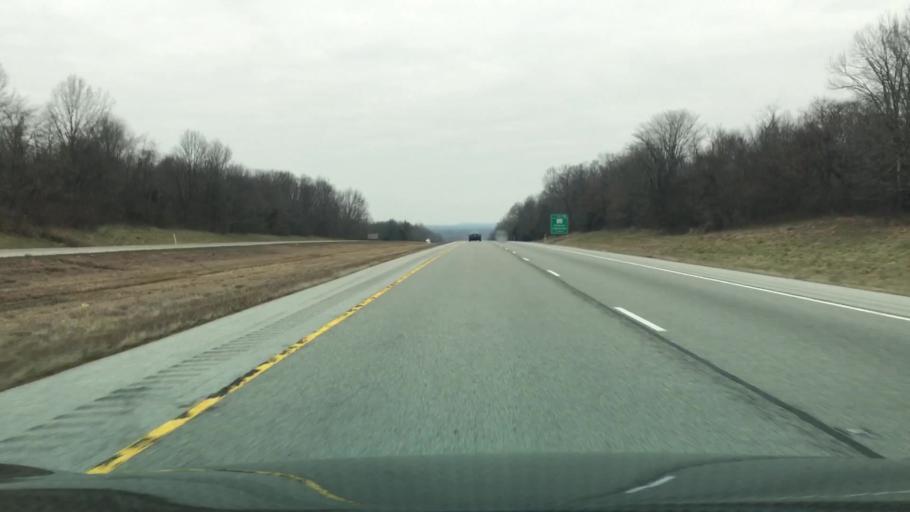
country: US
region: Illinois
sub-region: Johnson County
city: Vienna
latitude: 37.4004
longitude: -88.8526
